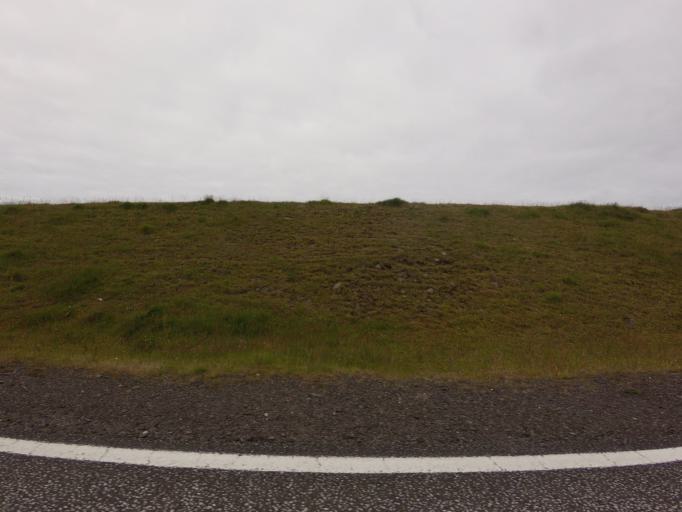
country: FO
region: Suduroy
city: Tvoroyri
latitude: 61.5316
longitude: -6.7995
